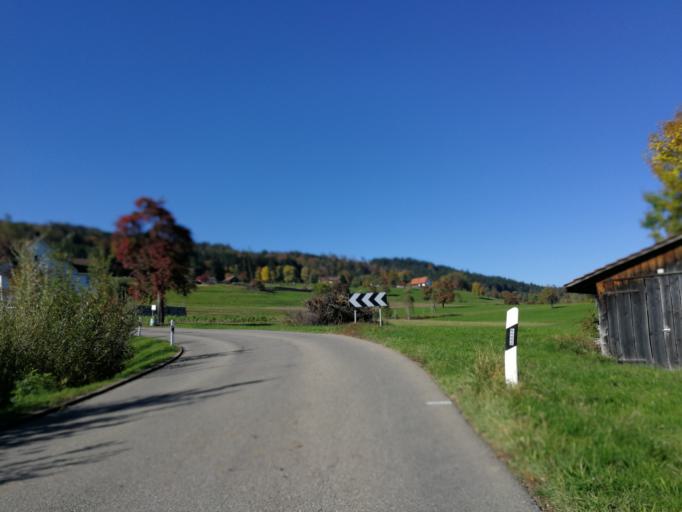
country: CH
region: Zurich
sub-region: Bezirk Uster
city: Hinteregg
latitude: 47.3007
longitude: 8.6833
